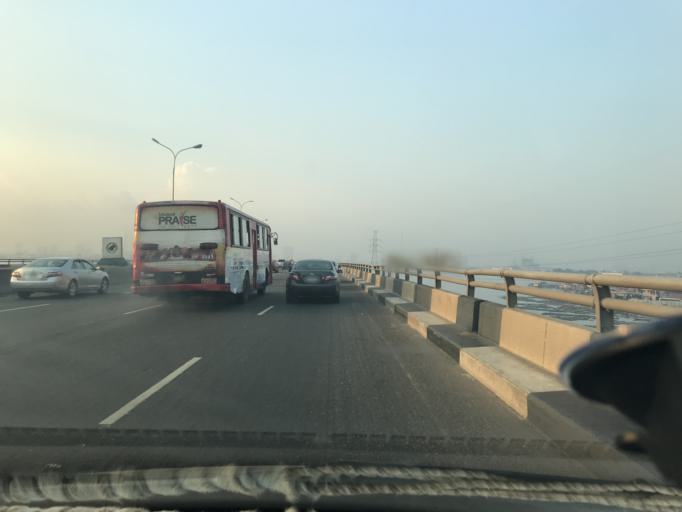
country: NG
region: Lagos
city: Ebute Metta
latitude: 6.4804
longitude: 3.3916
